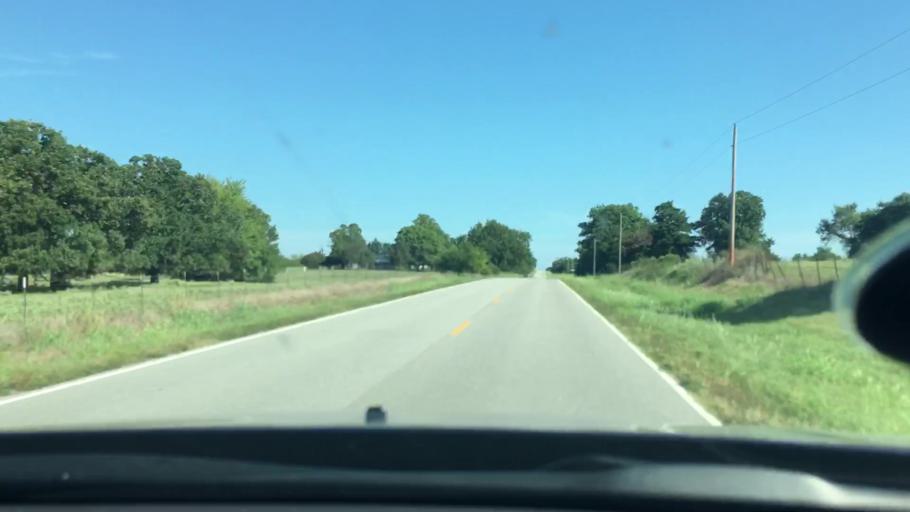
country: US
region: Oklahoma
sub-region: Johnston County
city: Tishomingo
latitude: 34.2910
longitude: -96.5488
